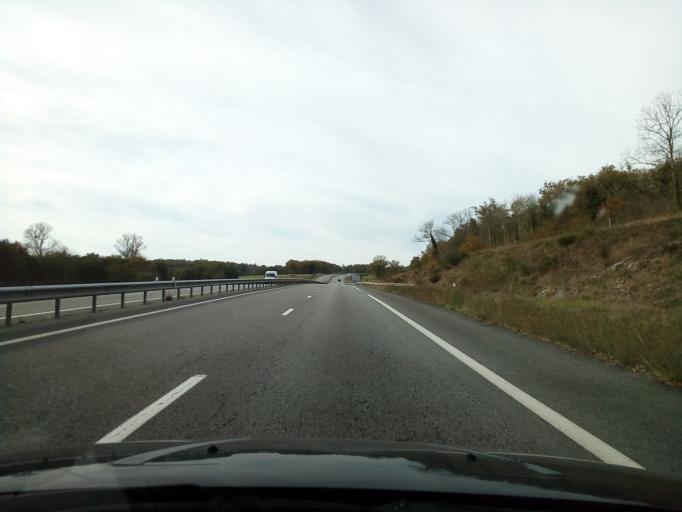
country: FR
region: Limousin
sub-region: Departement de la Creuse
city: Ajain
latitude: 46.2014
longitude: 2.1097
